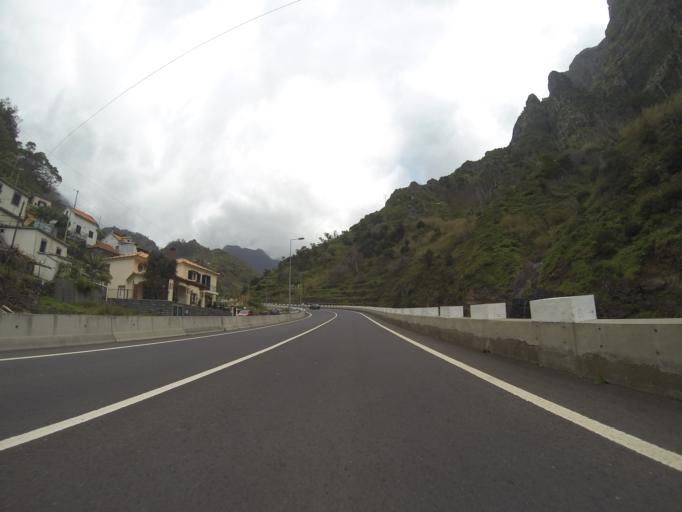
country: PT
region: Madeira
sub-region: Camara de Lobos
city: Curral das Freiras
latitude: 32.7243
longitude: -17.0276
